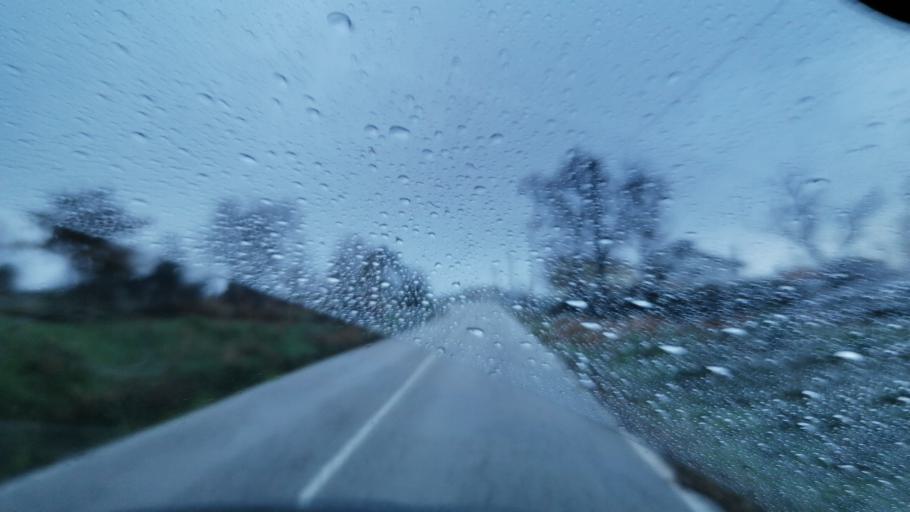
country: PT
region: Vila Real
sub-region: Murca
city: Murca
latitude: 41.4385
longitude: -7.5495
